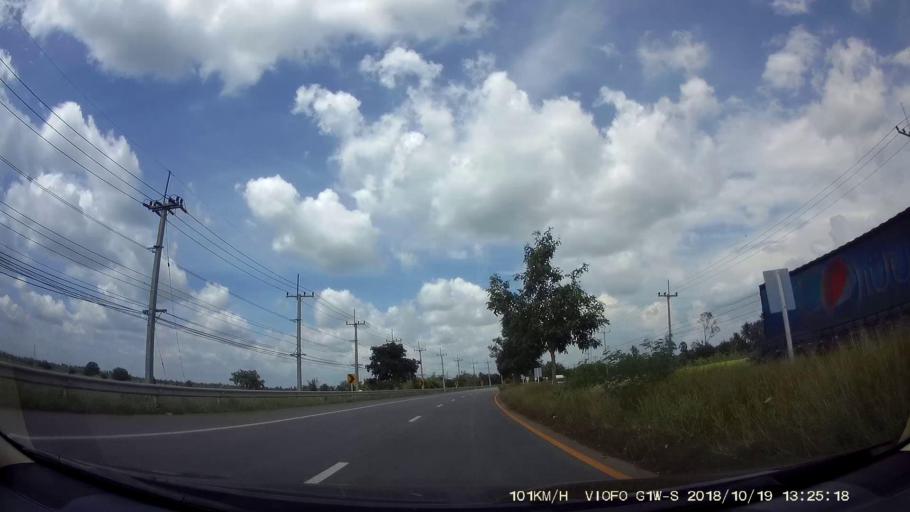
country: TH
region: Chaiyaphum
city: Chatturat
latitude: 15.5195
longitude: 101.8253
